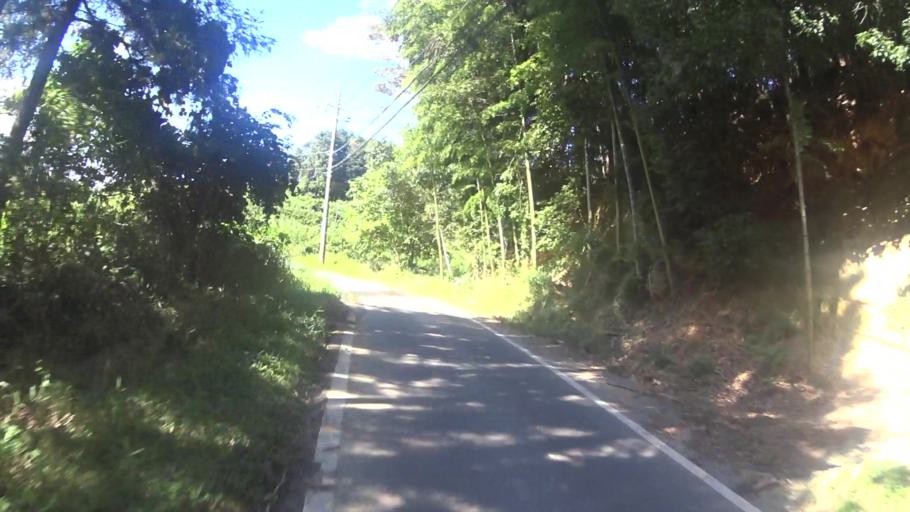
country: JP
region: Nara
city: Nara-shi
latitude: 34.7725
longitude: 135.9094
